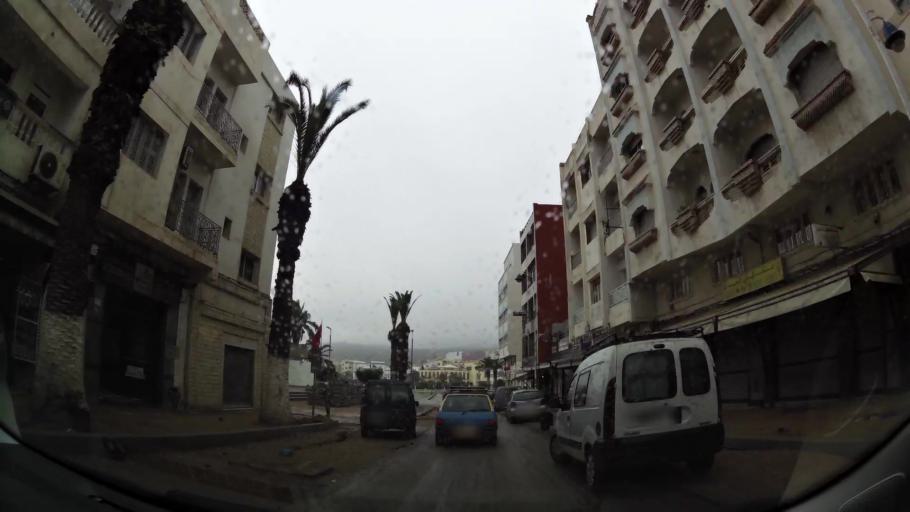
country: MA
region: Taza-Al Hoceima-Taounate
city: Al Hoceima
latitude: 35.2440
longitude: -3.9296
